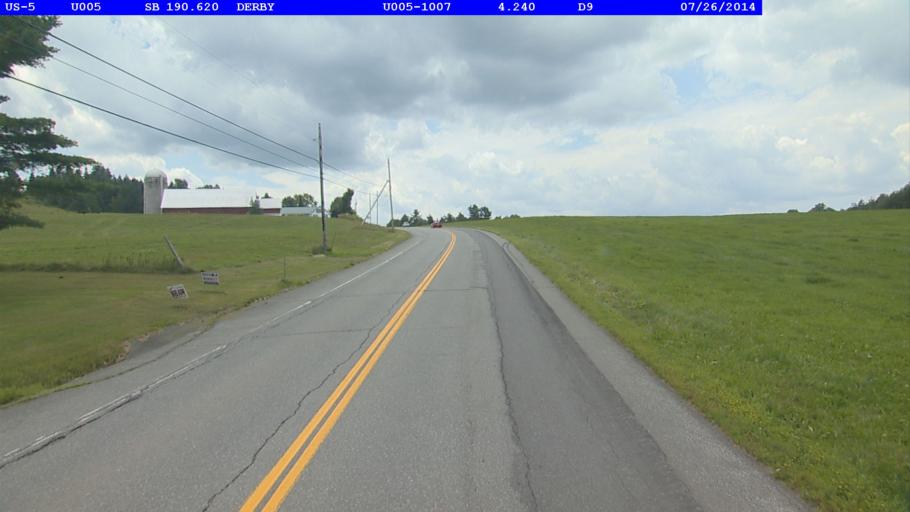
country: US
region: Vermont
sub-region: Orleans County
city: Newport
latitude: 44.9830
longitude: -72.1093
